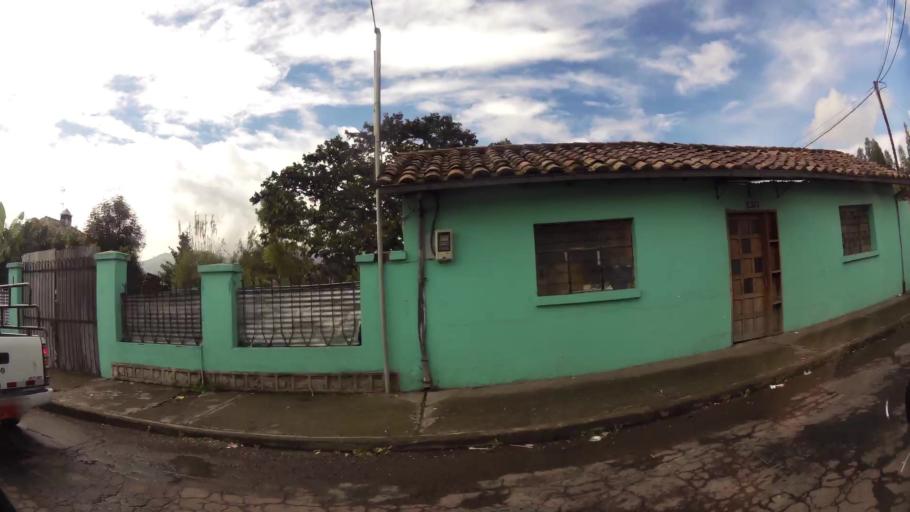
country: EC
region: Pichincha
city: Sangolqui
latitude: -0.3096
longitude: -78.4118
